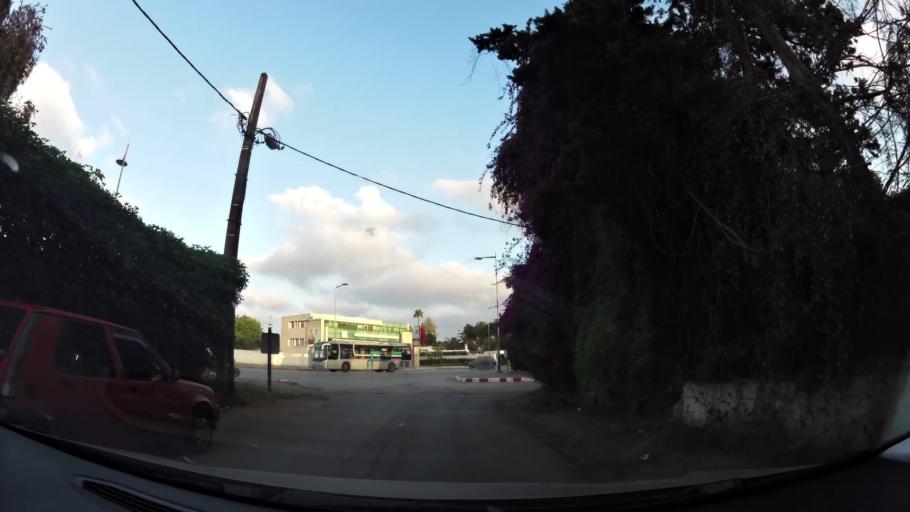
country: MA
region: Rabat-Sale-Zemmour-Zaer
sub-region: Rabat
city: Rabat
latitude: 33.9777
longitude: -6.8307
